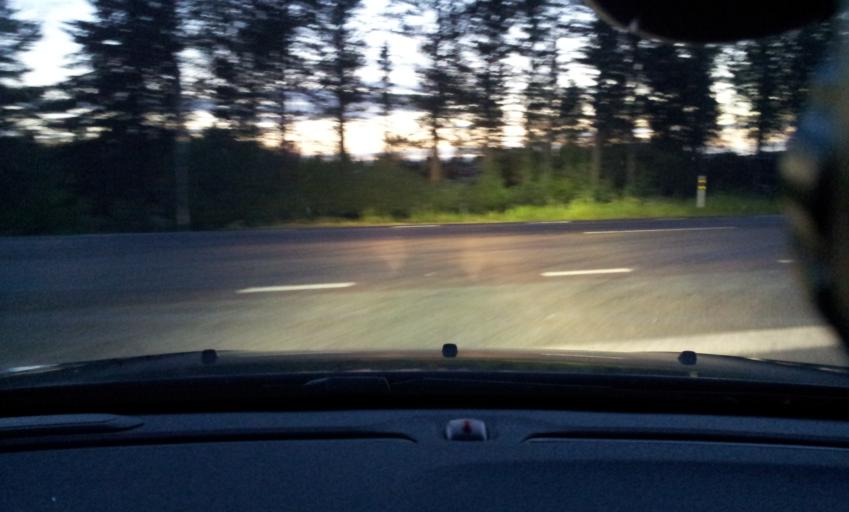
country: SE
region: Jaemtland
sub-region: Bergs Kommun
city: Hoverberg
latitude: 62.7939
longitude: 14.4821
